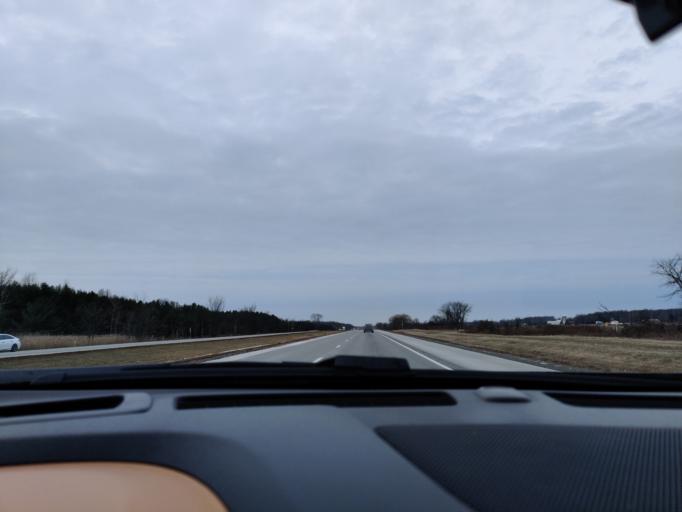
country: US
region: New York
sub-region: St. Lawrence County
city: Ogdensburg
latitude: 44.8802
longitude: -75.2862
